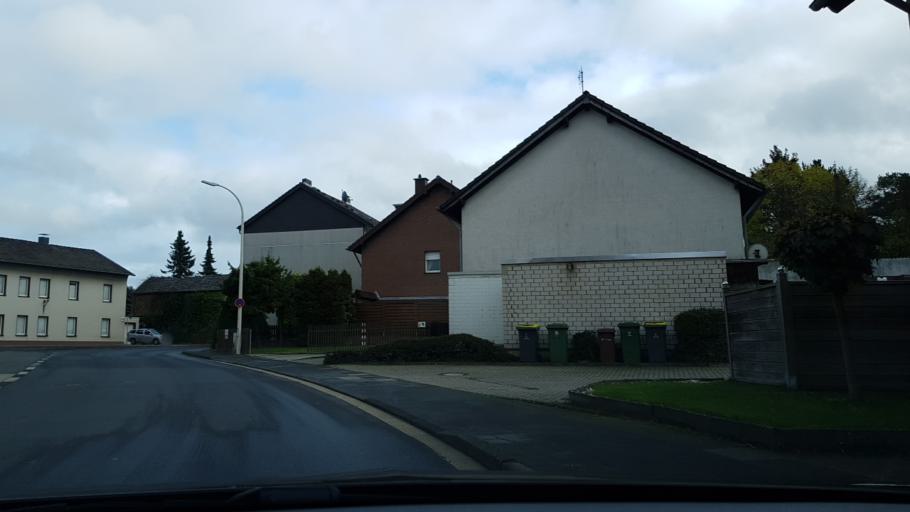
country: DE
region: North Rhine-Westphalia
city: Meckenheim
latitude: 50.5945
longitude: 7.0081
